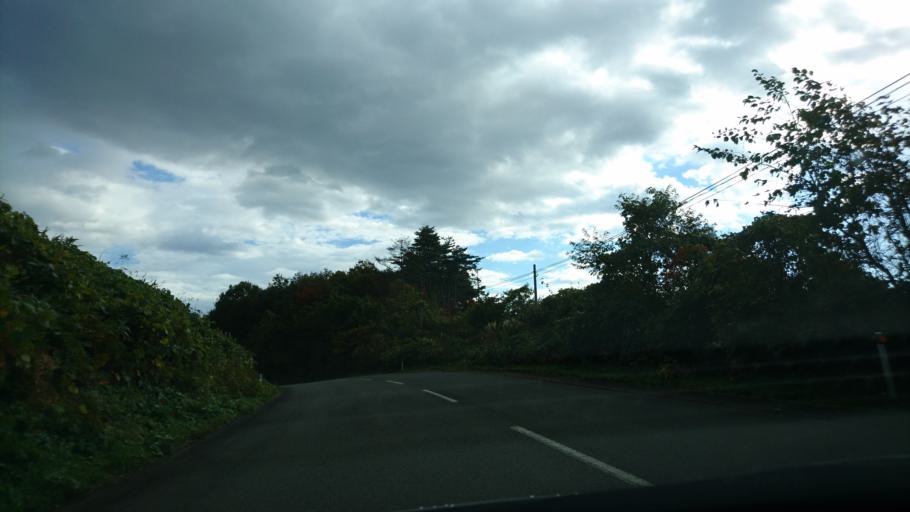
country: JP
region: Iwate
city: Mizusawa
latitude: 39.1002
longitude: 140.9850
